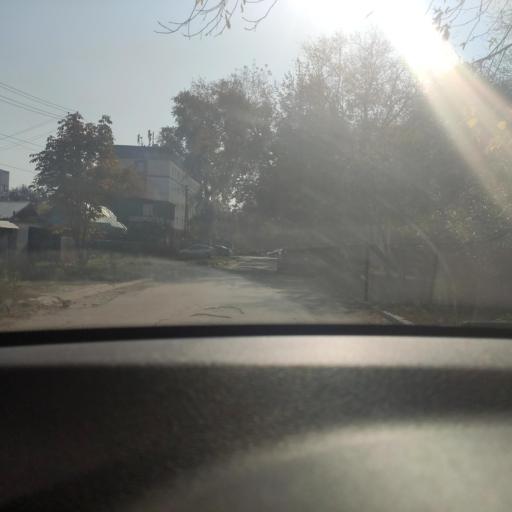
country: RU
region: Samara
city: Samara
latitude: 53.2027
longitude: 50.1941
